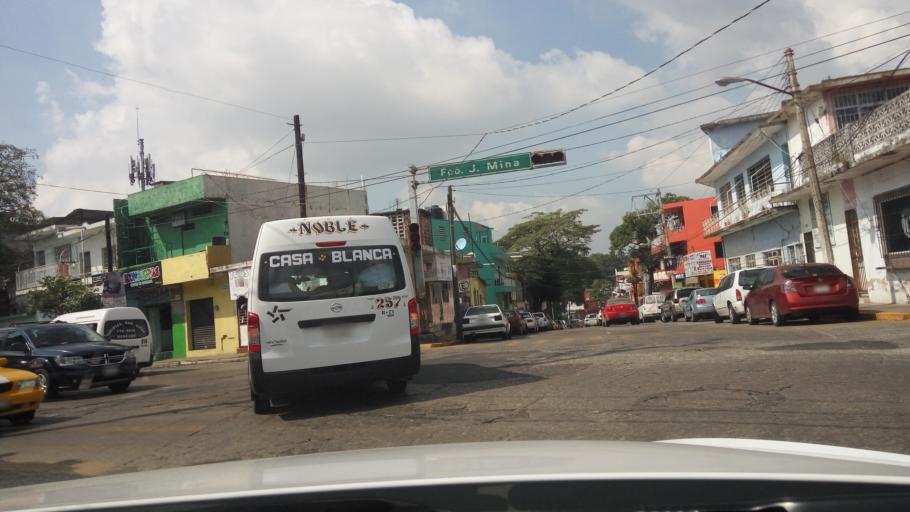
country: MX
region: Tabasco
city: Villahermosa
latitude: 17.9910
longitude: -92.9240
